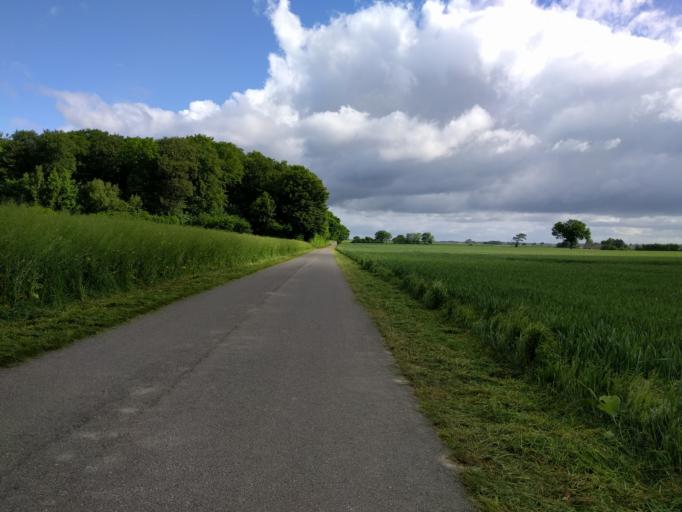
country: DK
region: South Denmark
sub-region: Kerteminde Kommune
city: Kerteminde
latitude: 55.4222
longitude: 10.6276
